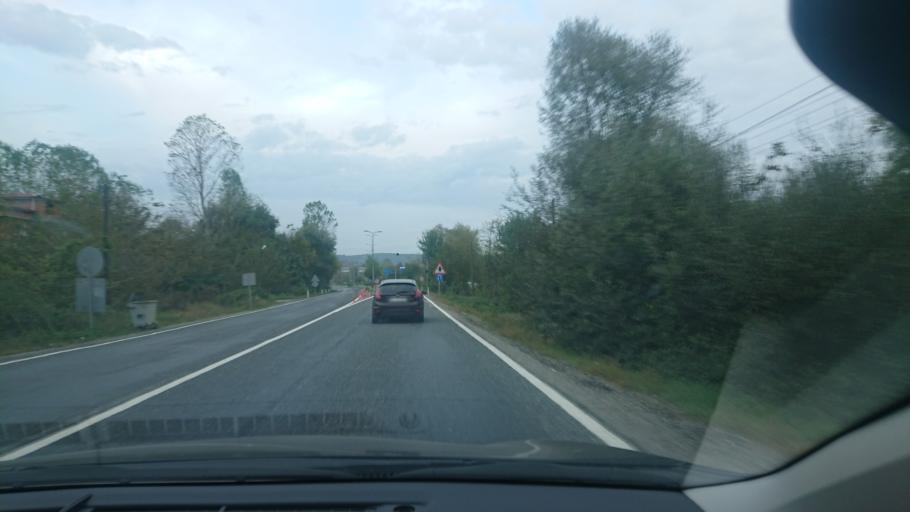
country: TR
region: Zonguldak
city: Gokcebey
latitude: 41.2989
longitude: 32.1228
